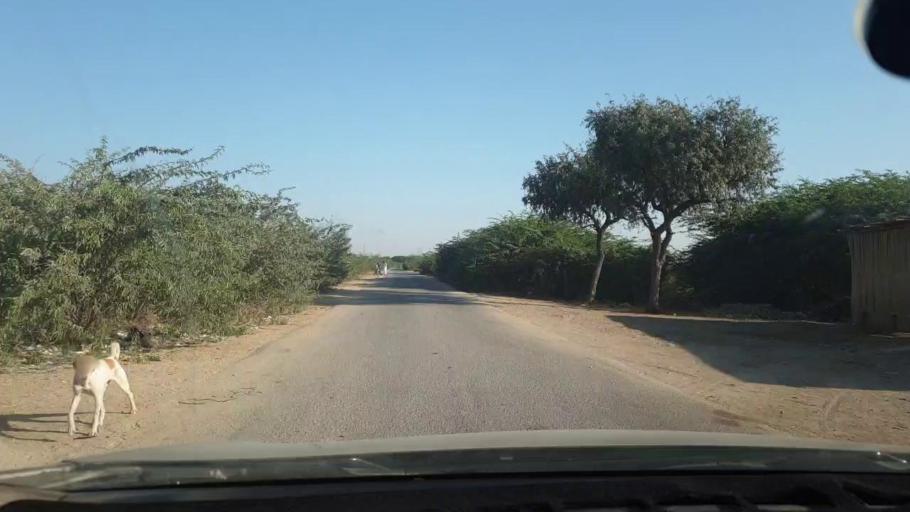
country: PK
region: Sindh
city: Malir Cantonment
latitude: 25.1451
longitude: 67.1868
